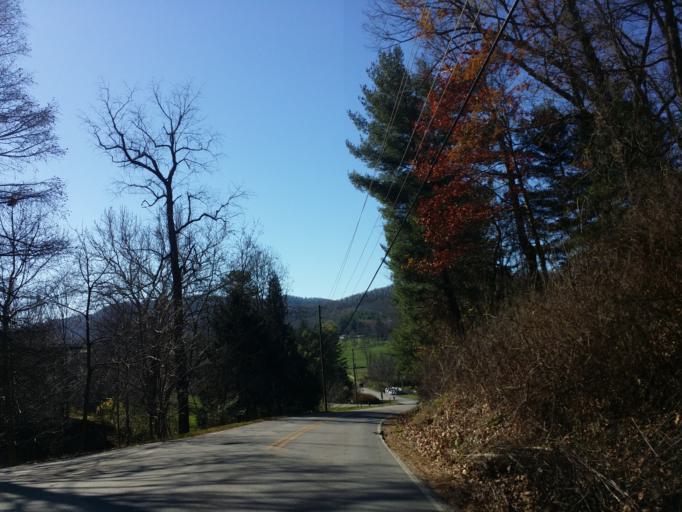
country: US
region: North Carolina
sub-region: Buncombe County
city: Swannanoa
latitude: 35.6110
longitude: -82.4429
